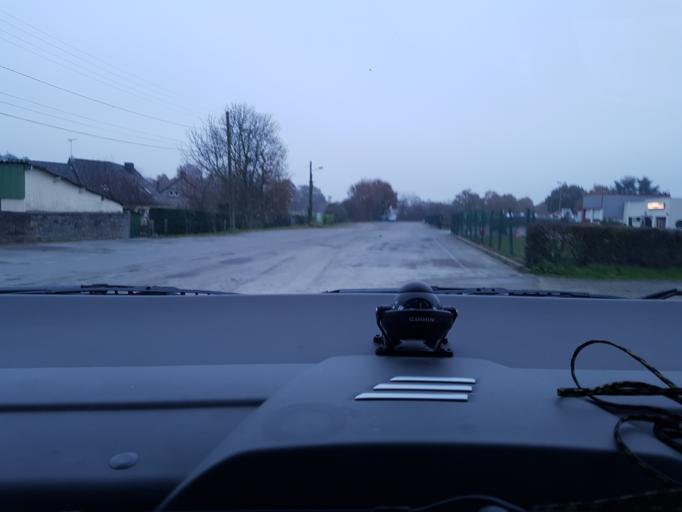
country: FR
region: Brittany
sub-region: Departement d'Ille-et-Vilaine
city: Saint-Brice-en-Cogles
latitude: 48.4069
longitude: -1.3688
